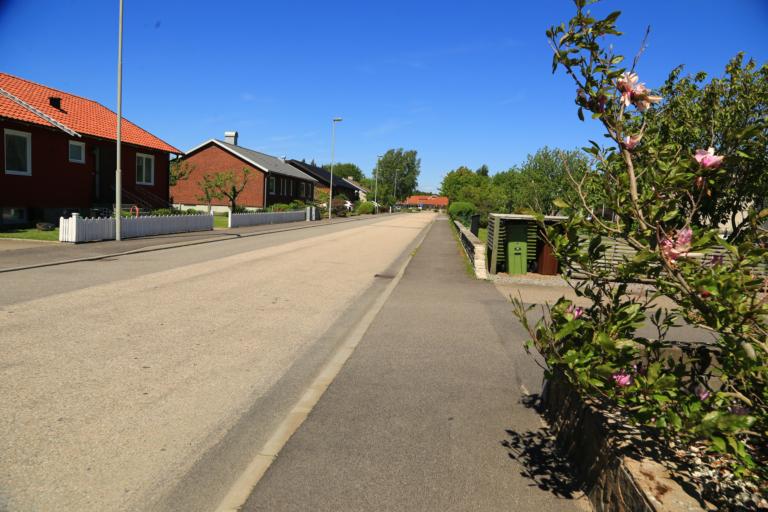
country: SE
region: Halland
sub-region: Varbergs Kommun
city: Varberg
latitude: 57.1099
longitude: 12.2796
